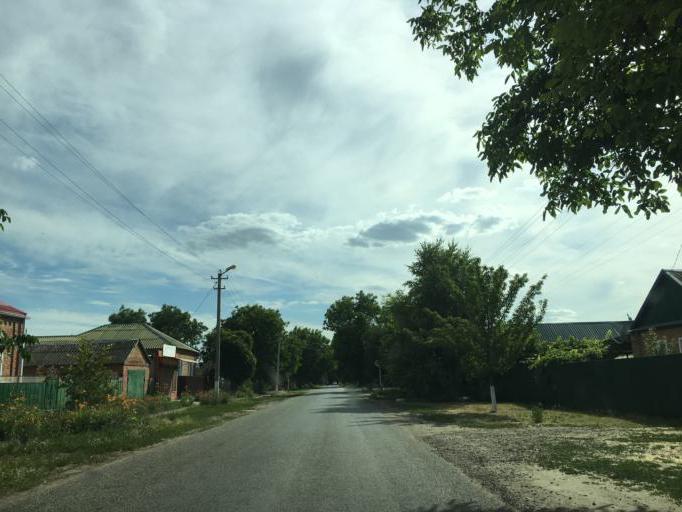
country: RU
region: Krasnodarskiy
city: Kushchevskaya
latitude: 46.5509
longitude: 39.6208
